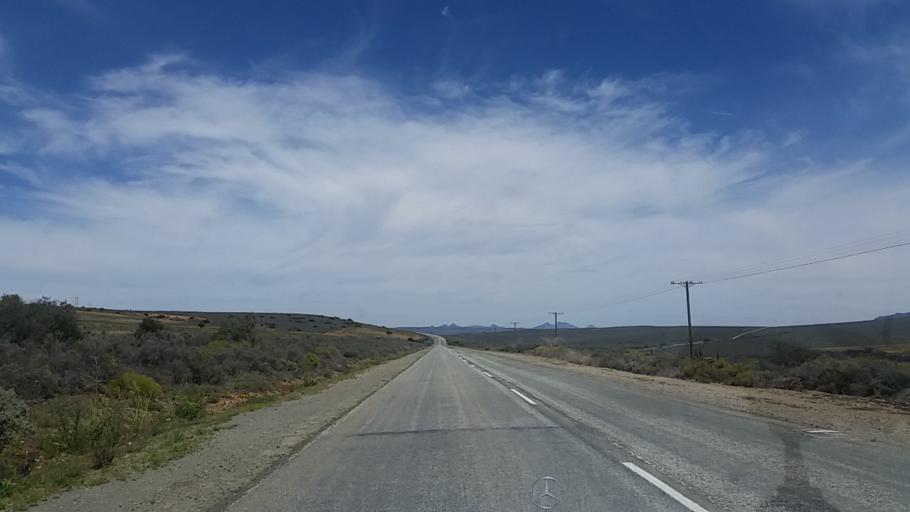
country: ZA
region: Western Cape
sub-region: Eden District Municipality
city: Knysna
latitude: -33.6233
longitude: 23.1361
